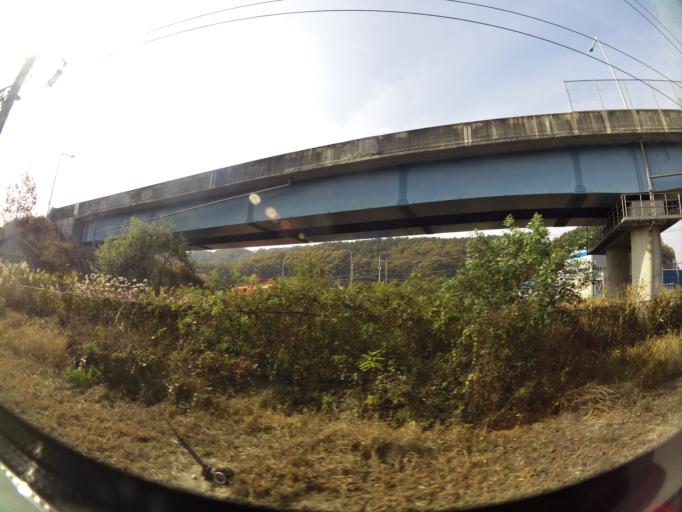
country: KR
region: Chungcheongbuk-do
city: Cheongju-si
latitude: 36.6316
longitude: 127.2893
